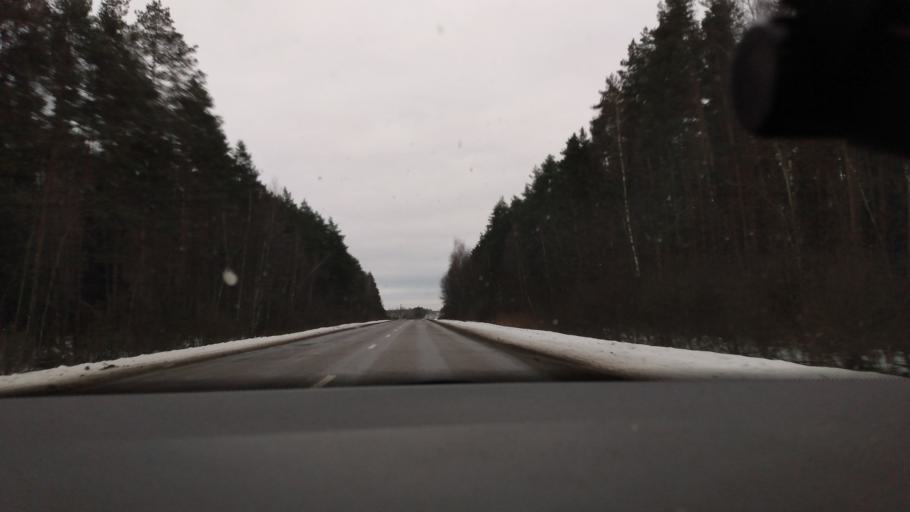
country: RU
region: Moskovskaya
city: Yegor'yevsk
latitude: 55.4277
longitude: 39.0332
